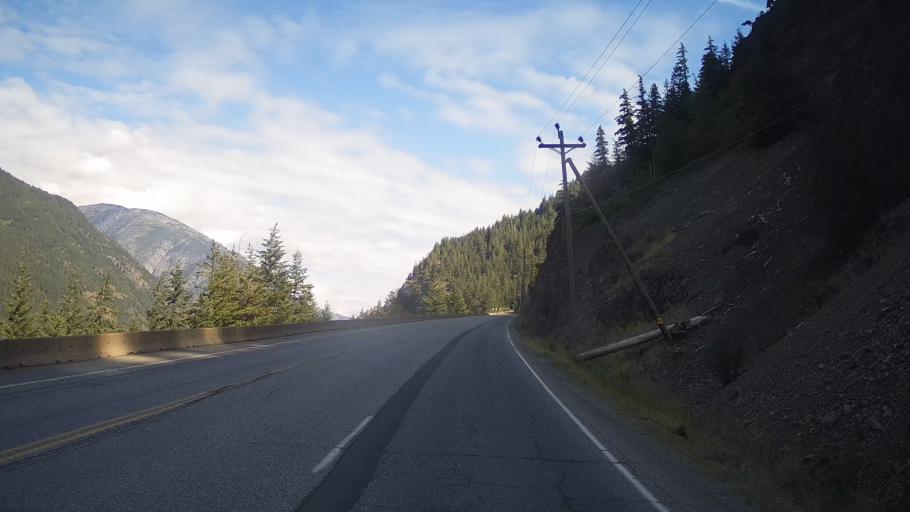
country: CA
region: British Columbia
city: Hope
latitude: 50.0687
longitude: -121.5456
